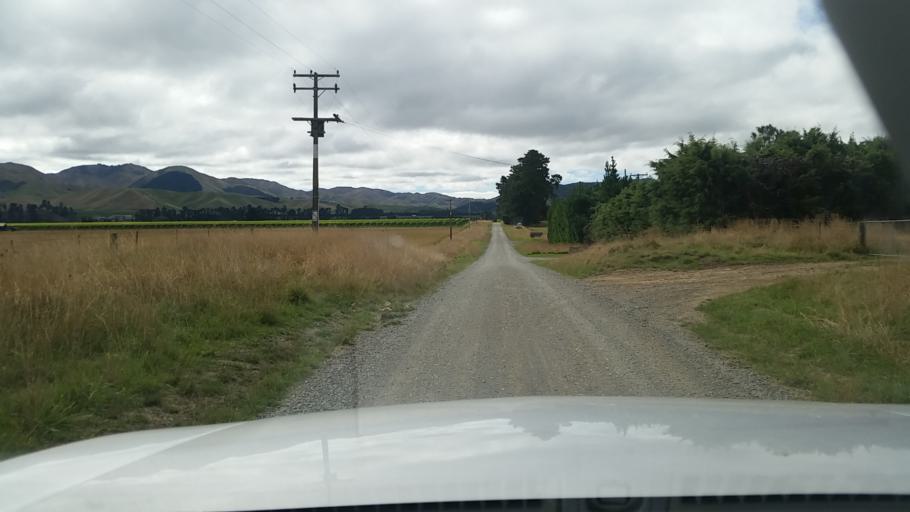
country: NZ
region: Marlborough
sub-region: Marlborough District
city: Blenheim
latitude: -41.6780
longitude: 174.0386
